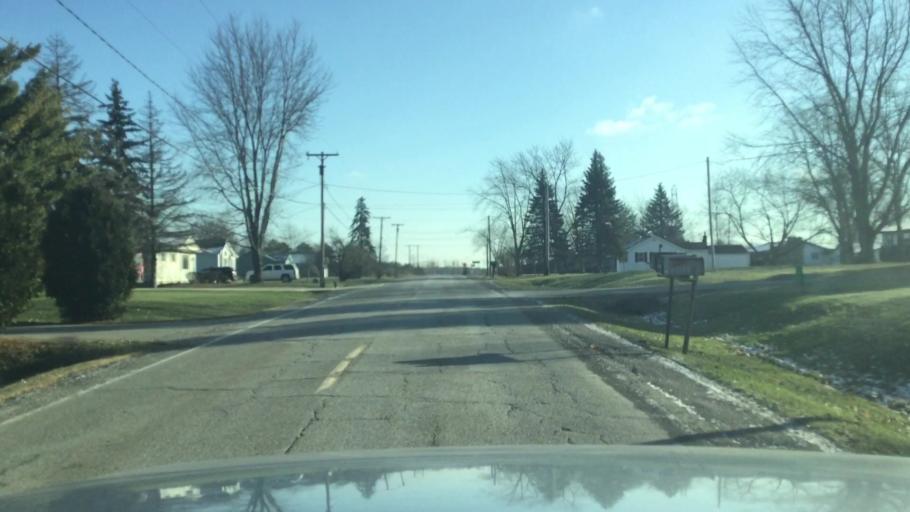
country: US
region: Michigan
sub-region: Genesee County
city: Grand Blanc
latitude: 42.9355
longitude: -83.6561
